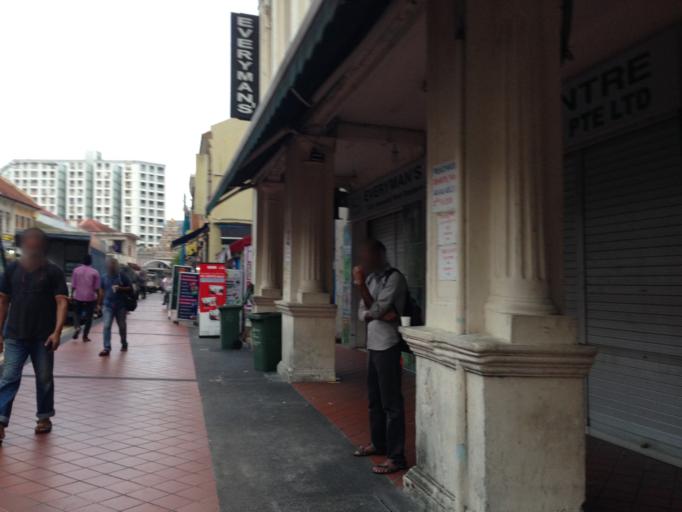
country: SG
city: Singapore
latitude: 1.3076
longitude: 103.8538
